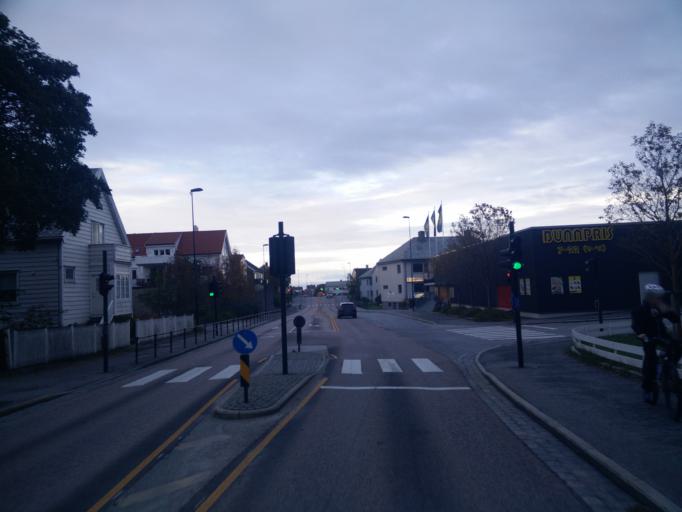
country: NO
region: More og Romsdal
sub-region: Kristiansund
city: Kristiansund
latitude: 63.1186
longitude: 7.7232
